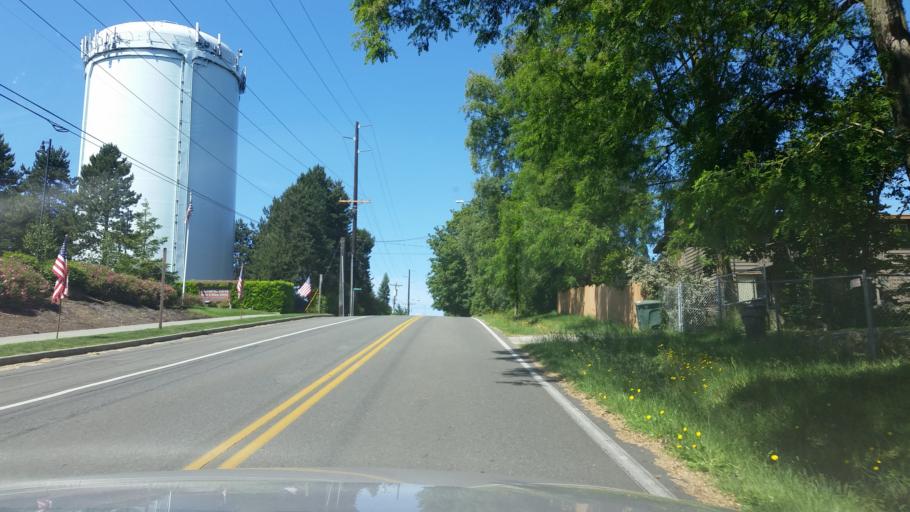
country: US
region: Washington
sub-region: Snohomish County
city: Esperance
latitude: 47.7924
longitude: -122.3427
